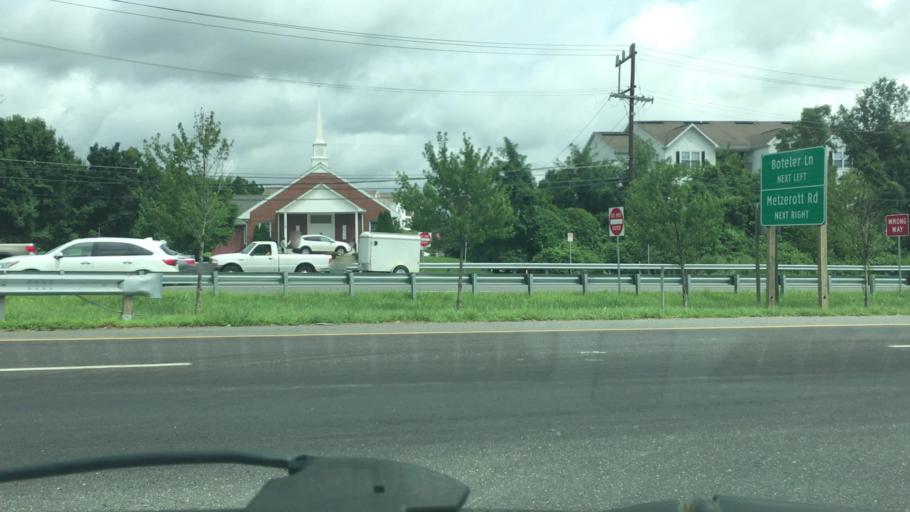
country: US
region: Maryland
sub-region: Prince George's County
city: College Park
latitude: 39.0008
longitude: -76.9423
